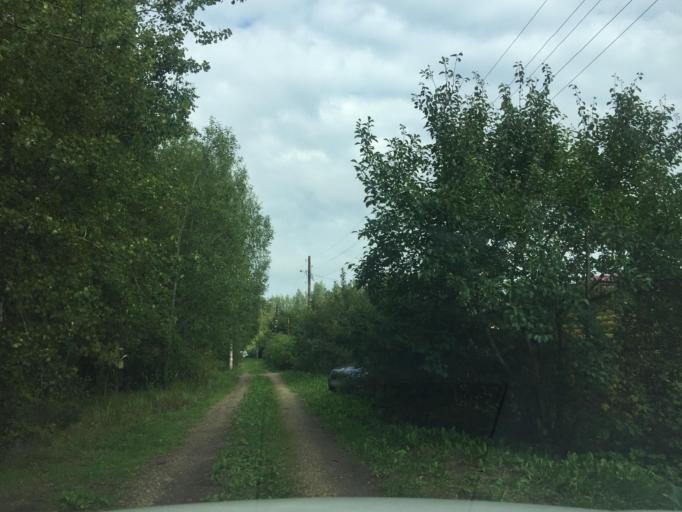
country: RU
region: Leningrad
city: Siverskiy
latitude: 59.2969
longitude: 30.0239
